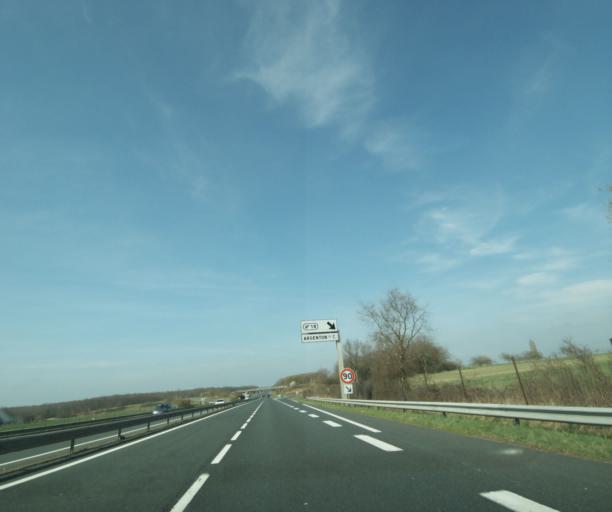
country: FR
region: Centre
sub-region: Departement de l'Indre
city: Argenton-sur-Creuse
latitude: 46.5679
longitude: 1.5031
